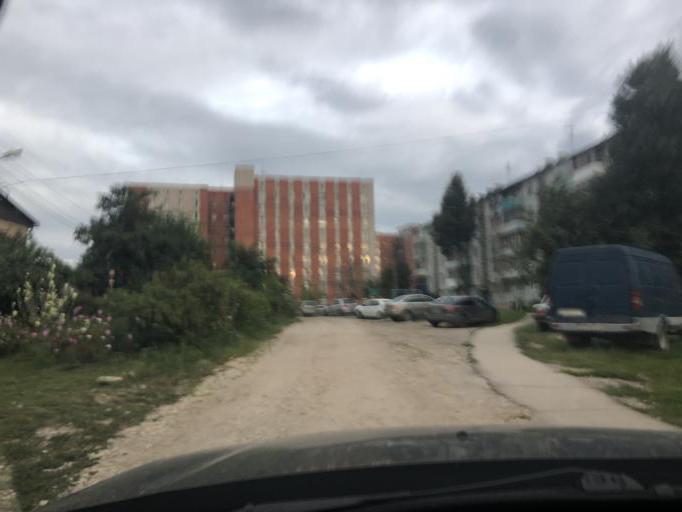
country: RU
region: Tula
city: Tula
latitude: 54.2064
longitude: 37.6996
